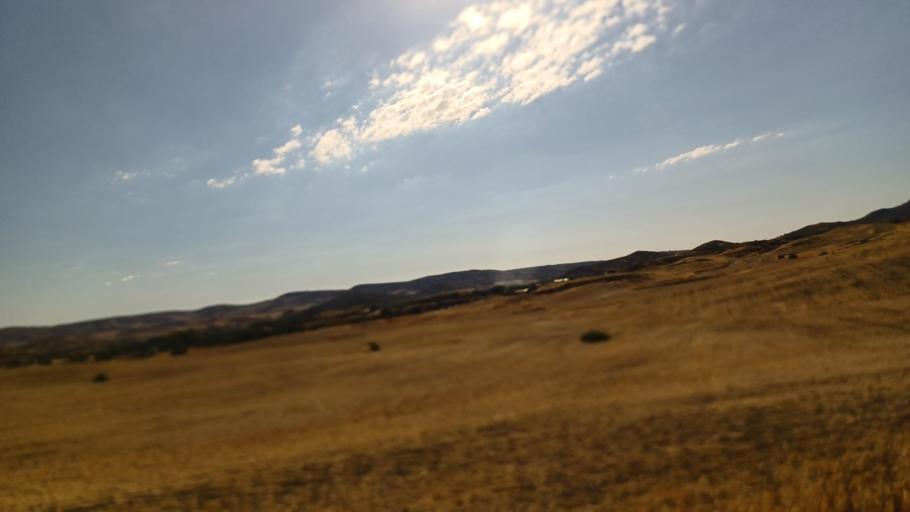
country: CY
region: Larnaka
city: Troulloi
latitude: 35.0103
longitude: 33.6084
